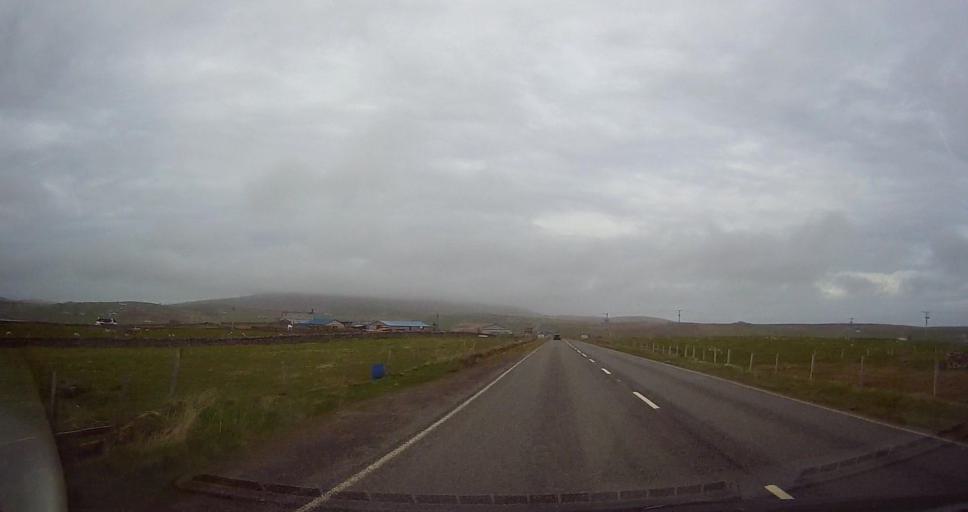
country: GB
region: Scotland
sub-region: Shetland Islands
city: Sandwick
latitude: 59.9161
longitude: -1.3007
